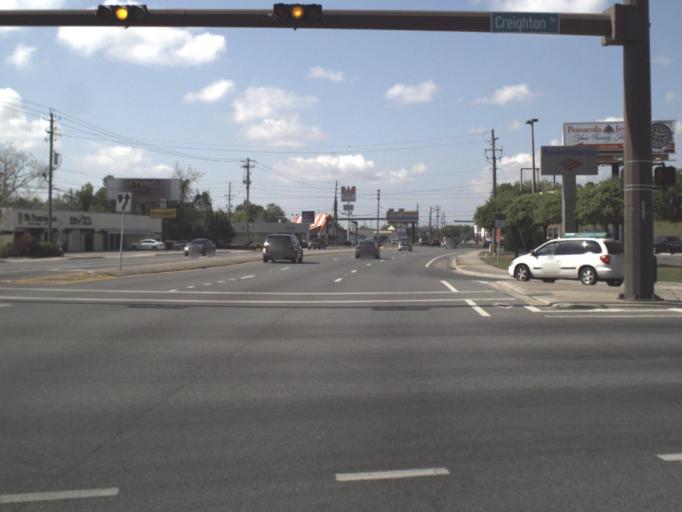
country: US
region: Florida
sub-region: Escambia County
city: Ferry Pass
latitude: 30.4961
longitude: -87.2221
